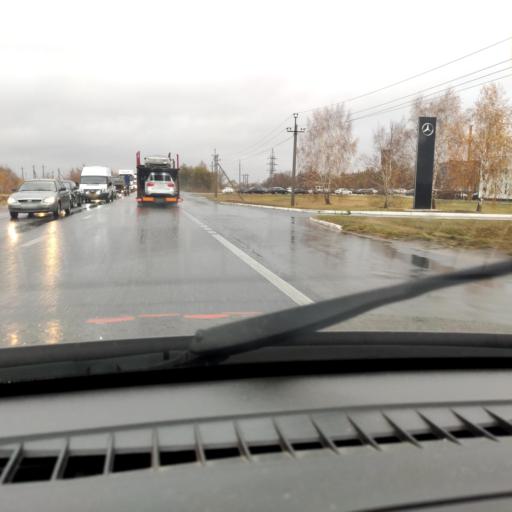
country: RU
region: Samara
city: Tol'yatti
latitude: 53.5671
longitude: 49.3486
